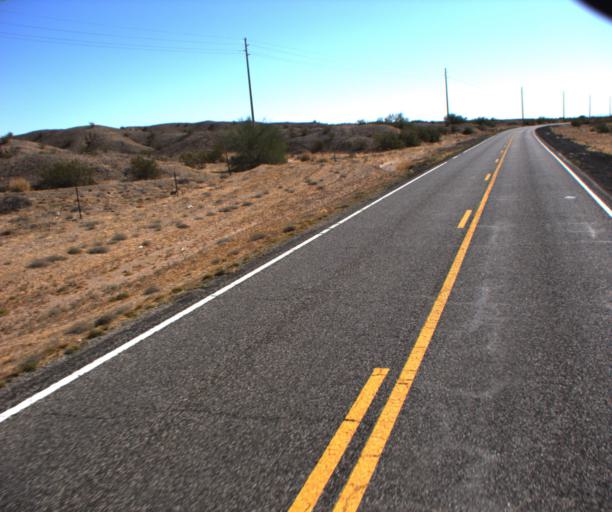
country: US
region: Arizona
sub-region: La Paz County
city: Parker
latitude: 33.9956
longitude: -114.1893
